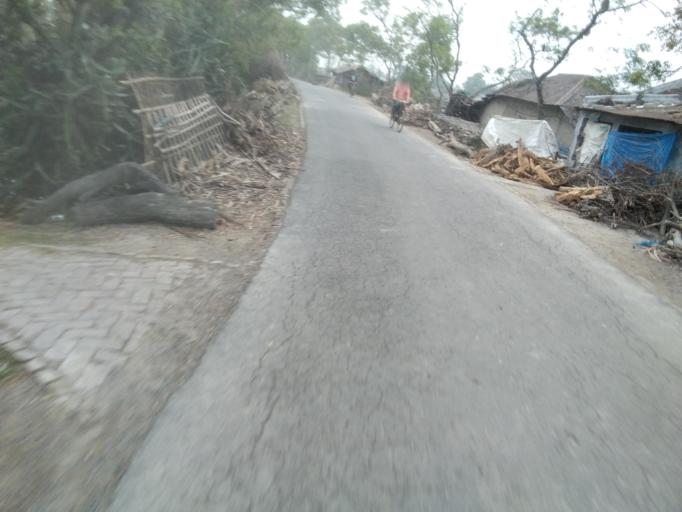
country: BD
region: Khulna
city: Satkhira
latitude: 22.5774
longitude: 89.0729
